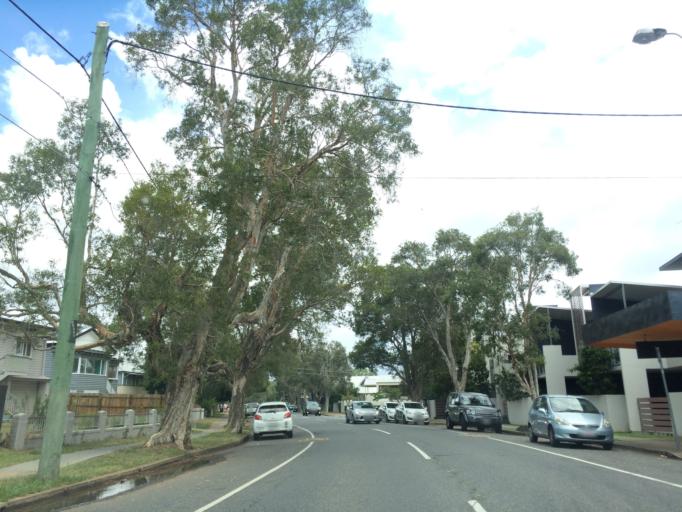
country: AU
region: Queensland
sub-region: Brisbane
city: Balmoral
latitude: -27.4598
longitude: 153.0632
